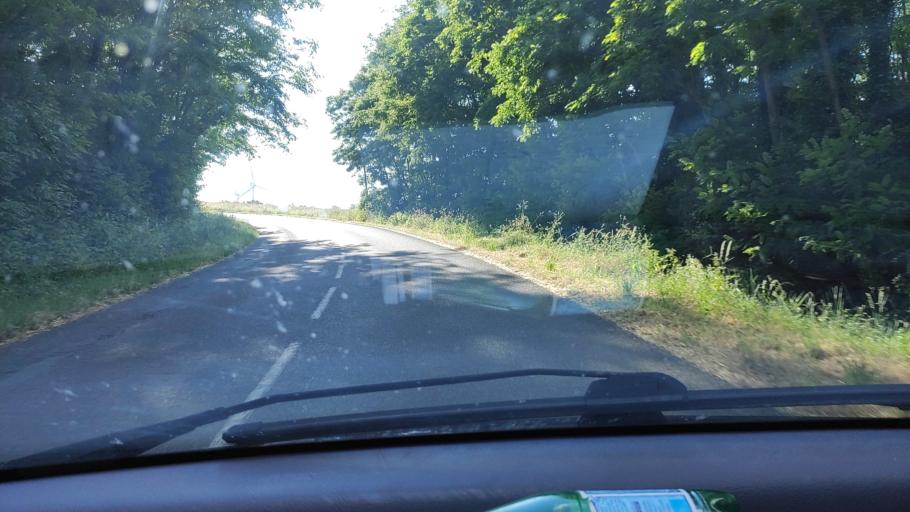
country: FR
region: Poitou-Charentes
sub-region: Departement des Deux-Sevres
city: Saint-Varent
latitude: 46.8598
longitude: -0.2039
